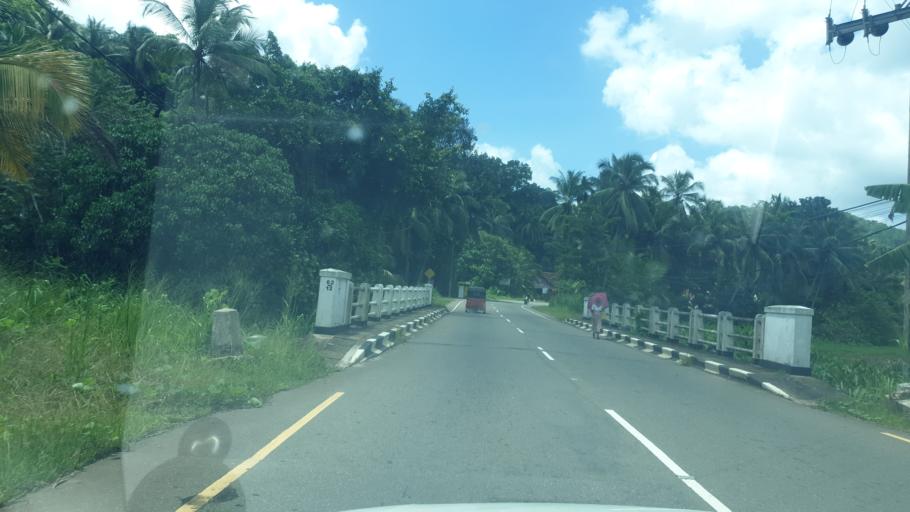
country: LK
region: Western
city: Horawala Junction
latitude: 6.5242
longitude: 80.1928
